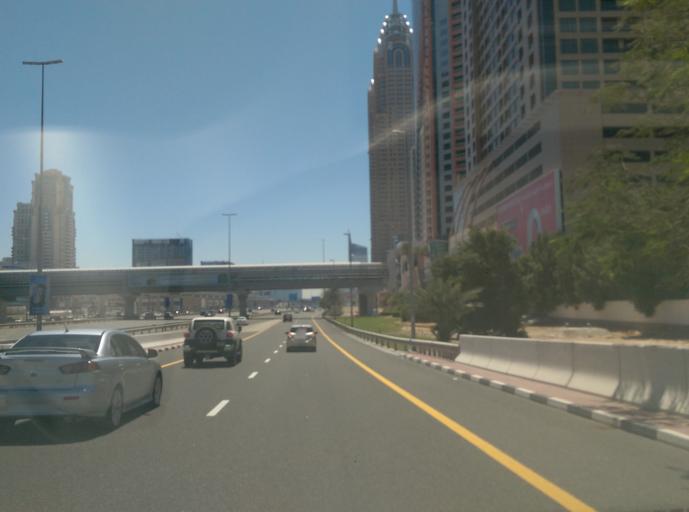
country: AE
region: Dubai
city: Dubai
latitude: 25.1035
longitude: 55.1737
